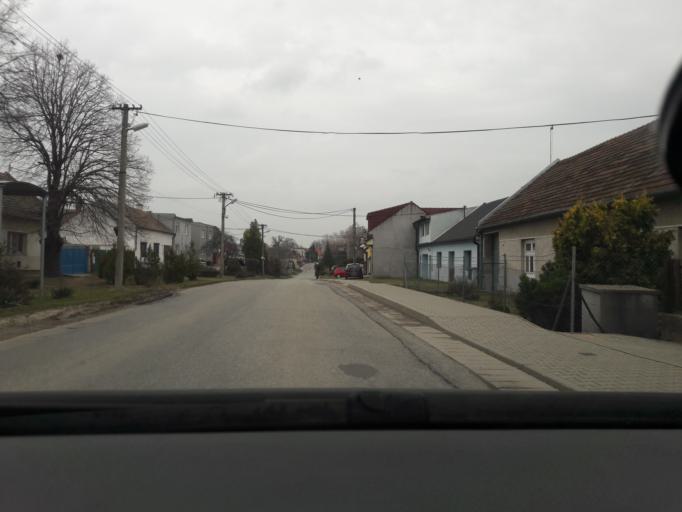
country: SK
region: Bratislavsky
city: Senec
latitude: 48.3080
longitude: 17.4452
